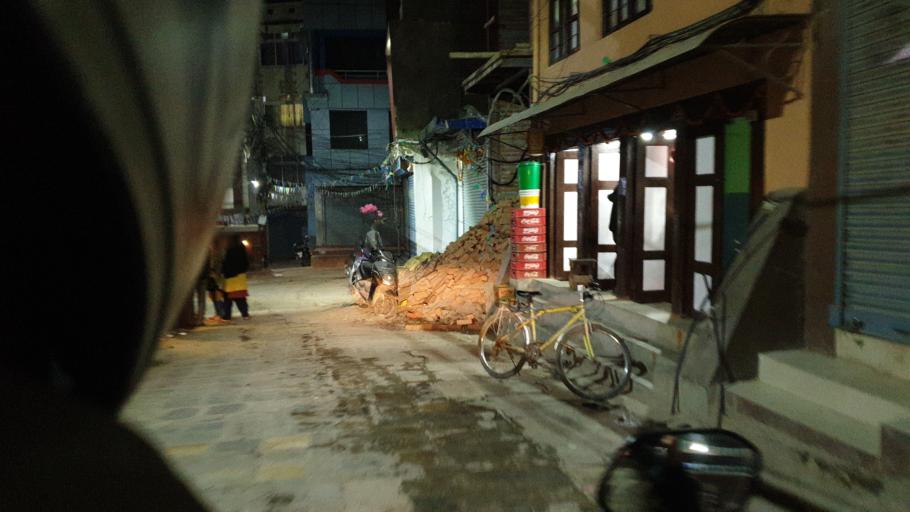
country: NP
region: Central Region
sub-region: Bagmati Zone
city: Kathmandu
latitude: 27.6976
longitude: 85.3084
